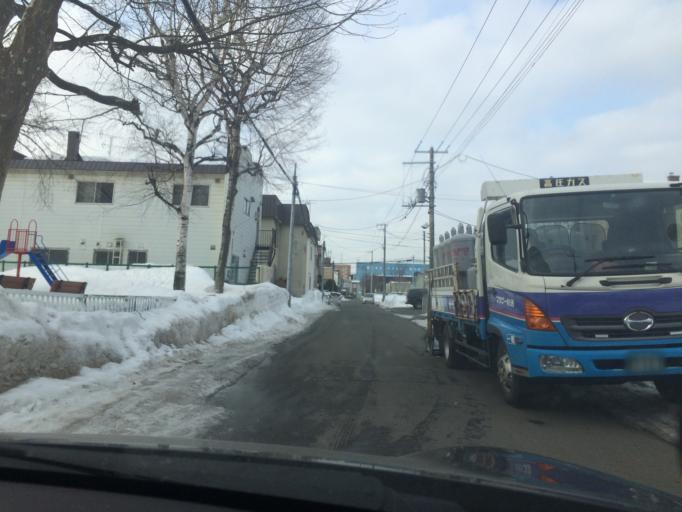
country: JP
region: Hokkaido
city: Sapporo
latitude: 43.0581
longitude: 141.4137
